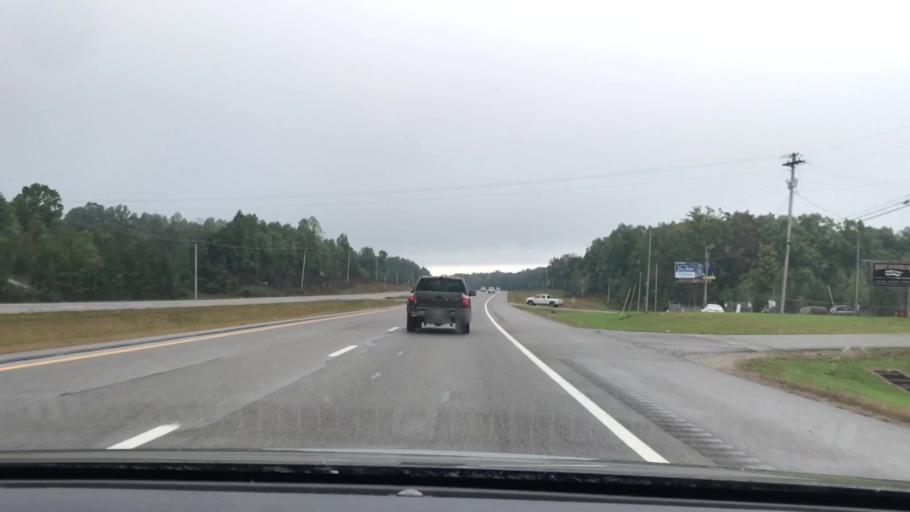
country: US
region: Tennessee
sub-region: Fentress County
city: Jamestown
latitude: 36.3620
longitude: -84.9471
